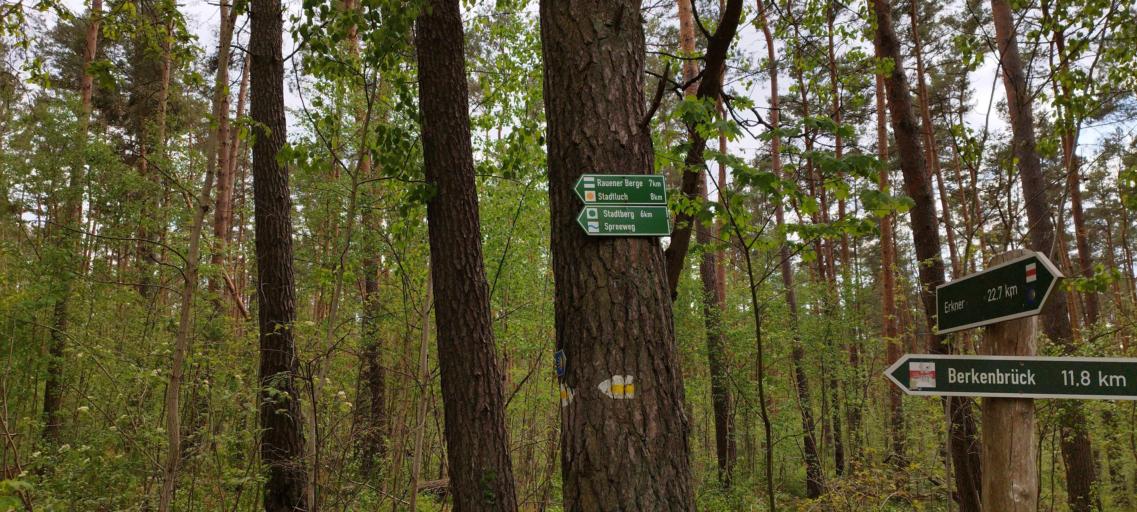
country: DE
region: Brandenburg
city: Rauen
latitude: 52.3668
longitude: 13.9928
